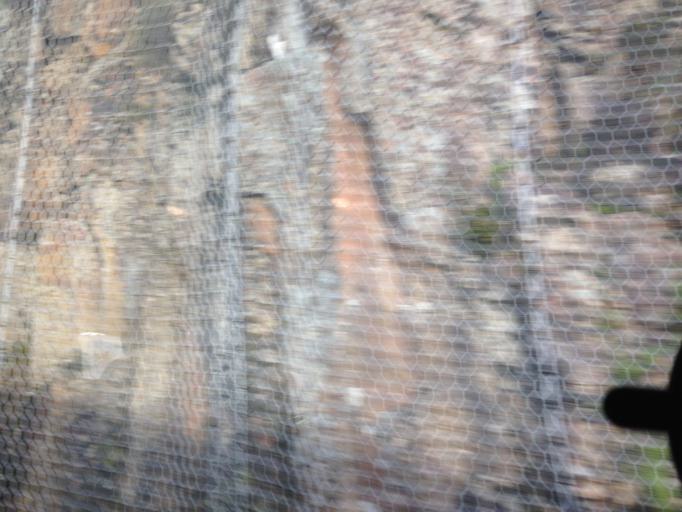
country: GB
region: Scotland
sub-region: Argyll and Bute
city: Garelochhead
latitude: 56.1664
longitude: -4.7818
